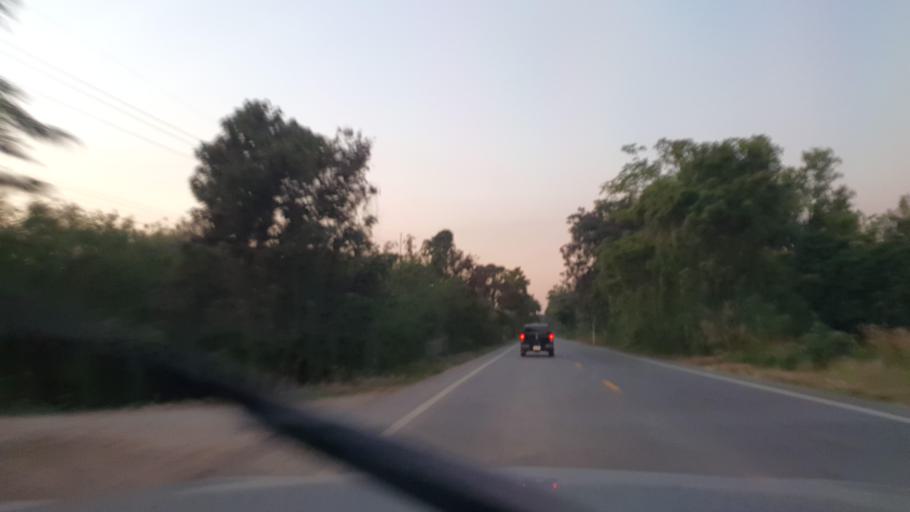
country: TH
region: Phayao
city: Dok Kham Tai
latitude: 19.1348
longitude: 100.0248
